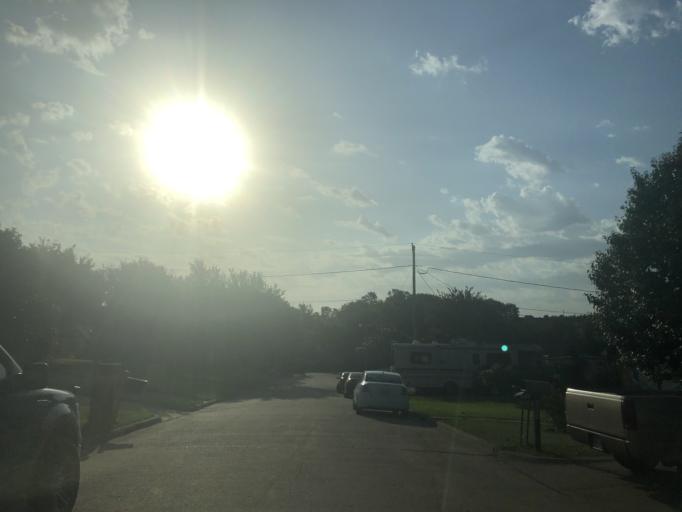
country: US
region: Texas
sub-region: Dallas County
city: Grand Prairie
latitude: 32.7686
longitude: -97.0308
